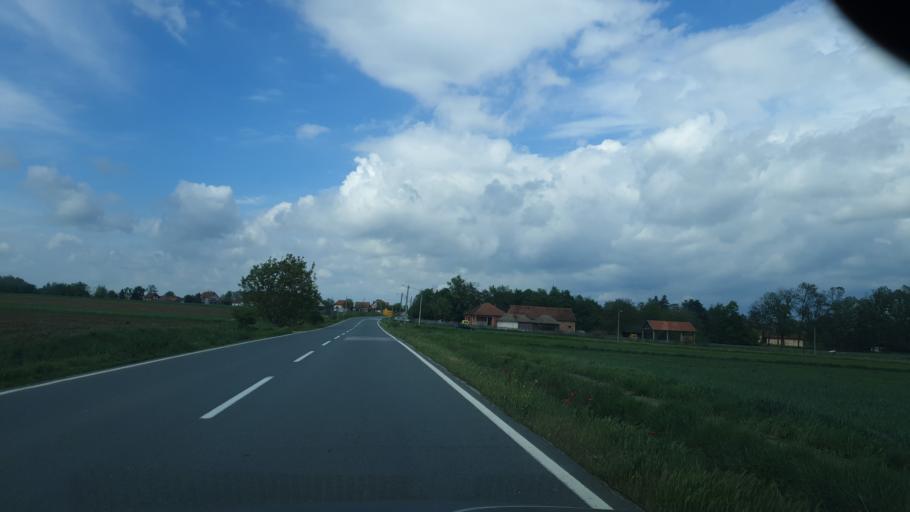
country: RS
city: Stubline
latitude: 44.5375
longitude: 20.1229
